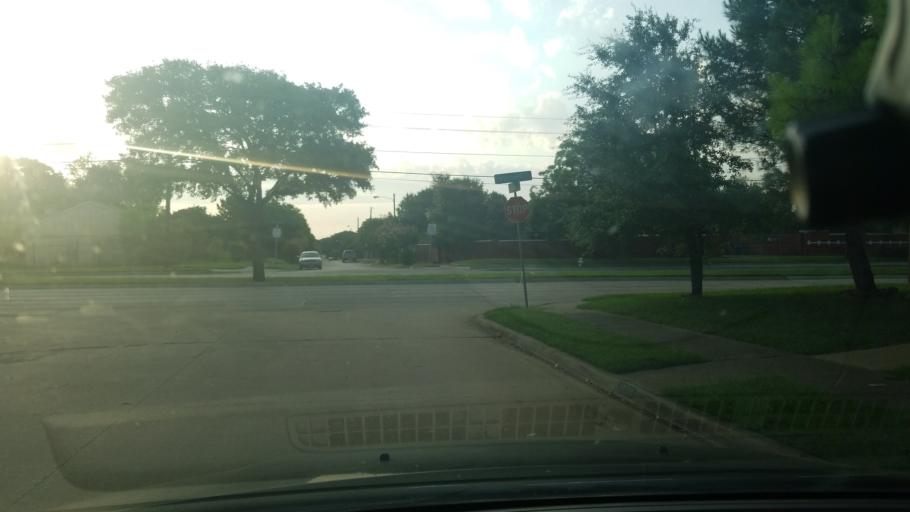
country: US
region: Texas
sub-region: Dallas County
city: Balch Springs
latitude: 32.7285
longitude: -96.6488
